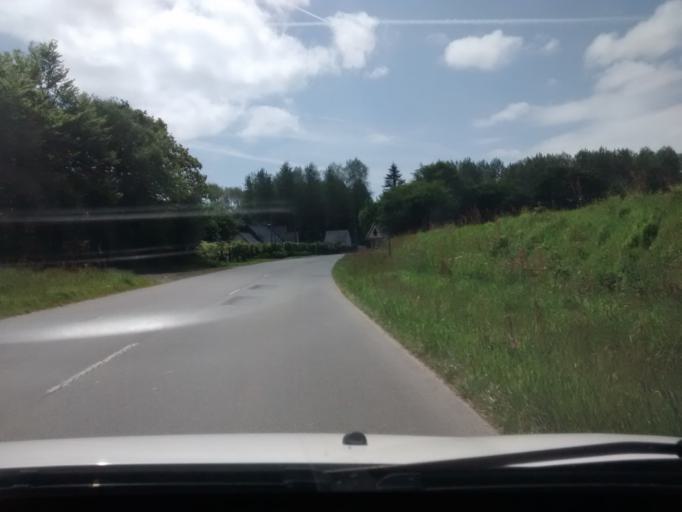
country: FR
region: Brittany
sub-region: Departement des Cotes-d'Armor
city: Louannec
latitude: 48.7745
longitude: -3.4182
